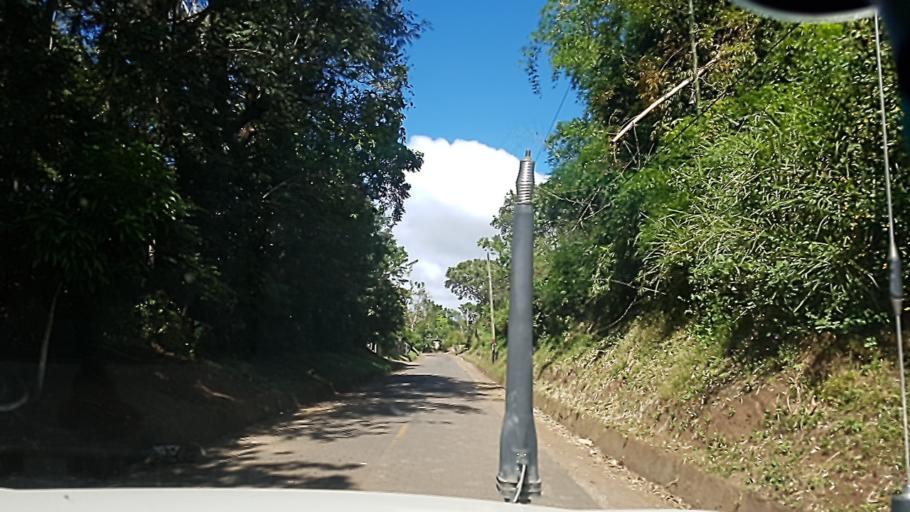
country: NI
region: Carazo
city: La Paz de Oriente
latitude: 11.8300
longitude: -86.1537
